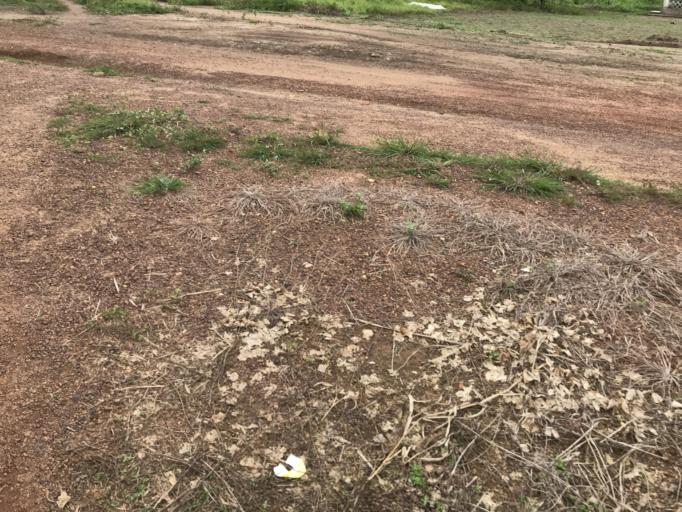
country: GN
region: Nzerekore
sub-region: Prefecture de Guekedou
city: Gueckedou
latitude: 8.4721
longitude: -10.2791
